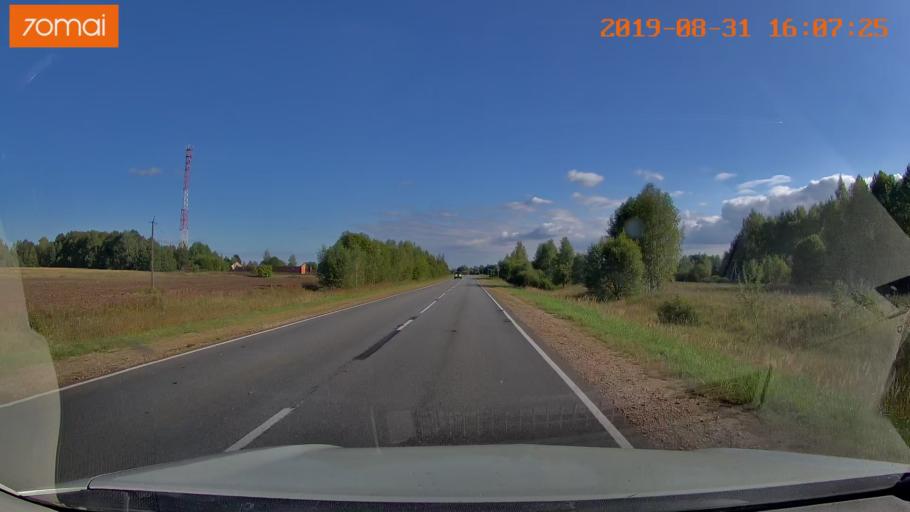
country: RU
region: Kaluga
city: Yukhnov
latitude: 54.6097
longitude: 35.3584
